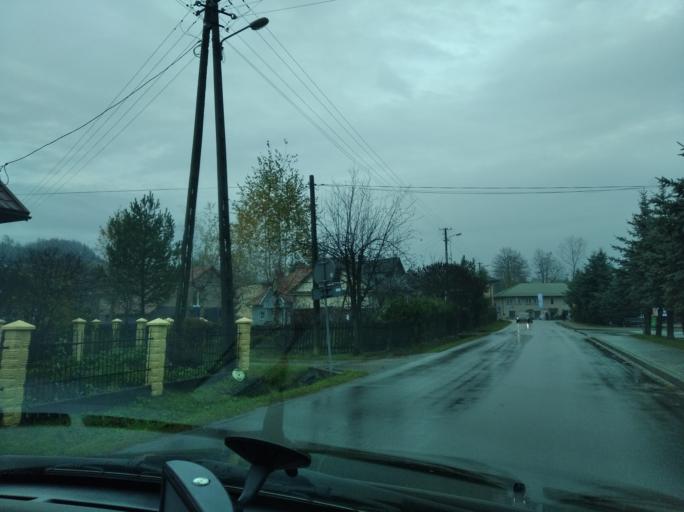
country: PL
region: Subcarpathian Voivodeship
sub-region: Powiat rzeszowski
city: Lubenia
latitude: 49.9256
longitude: 21.9365
